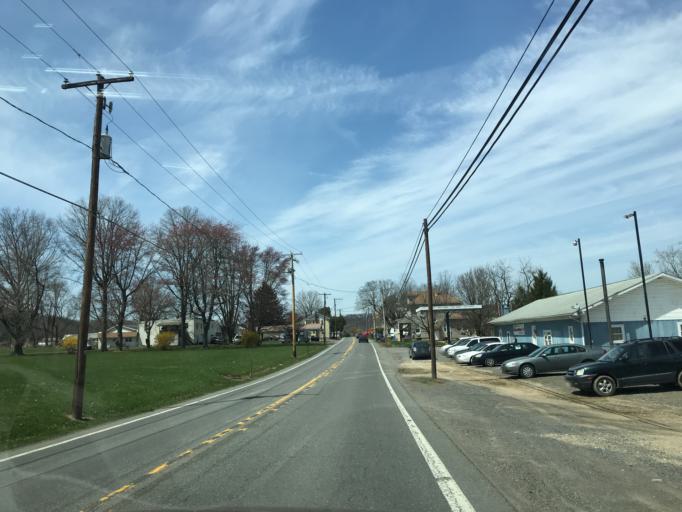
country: US
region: Pennsylvania
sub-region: Snyder County
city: Selinsgrove
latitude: 40.8133
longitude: -76.8680
